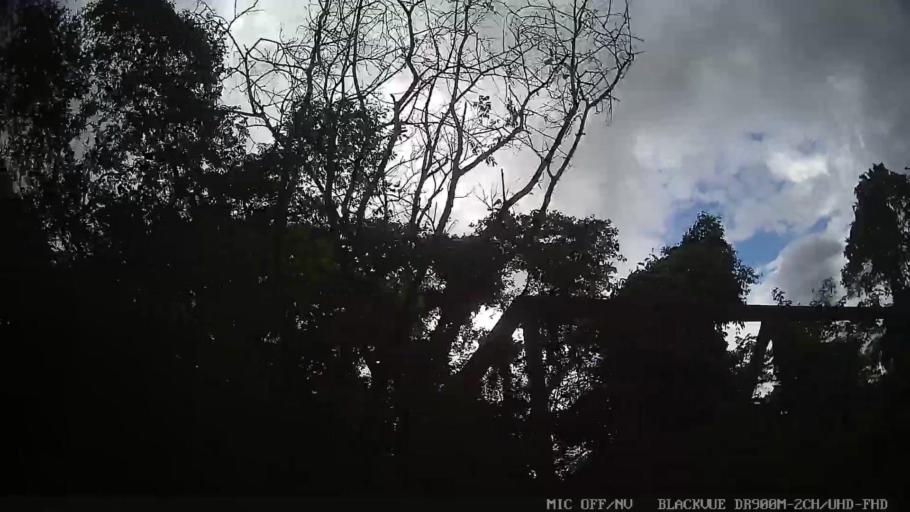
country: BR
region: Sao Paulo
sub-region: Jaguariuna
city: Jaguariuna
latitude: -22.6718
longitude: -46.9734
